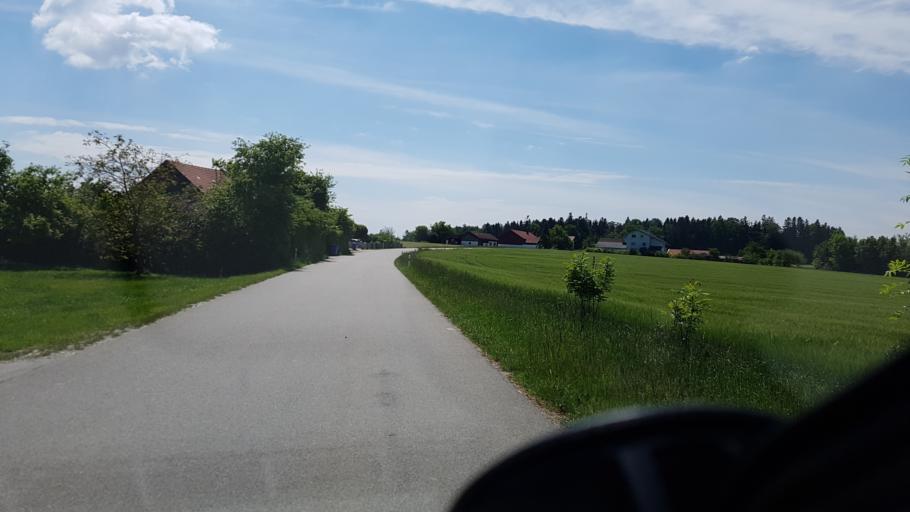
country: DE
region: Bavaria
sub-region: Lower Bavaria
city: Stubenberg
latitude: 48.3428
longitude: 13.0665
